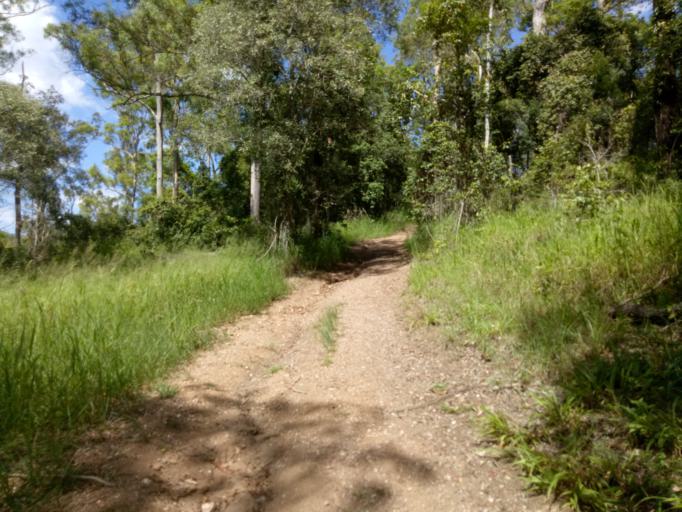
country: AU
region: Queensland
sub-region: Moreton Bay
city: Ferny Hills
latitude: -27.4472
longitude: 152.9113
